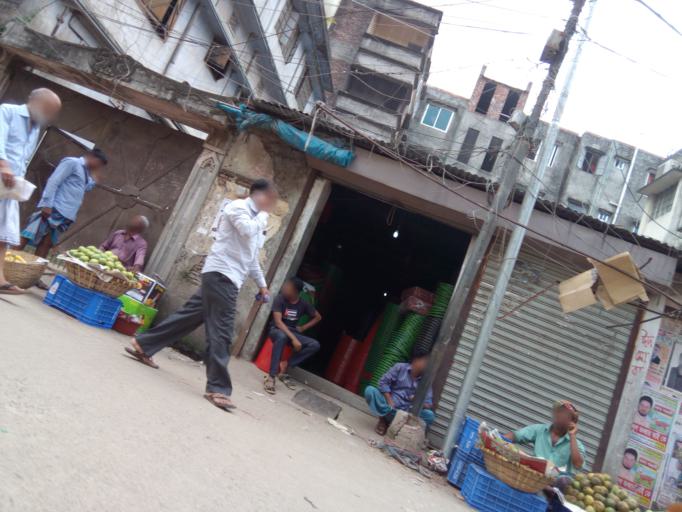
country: BD
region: Dhaka
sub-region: Dhaka
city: Dhaka
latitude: 23.7154
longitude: 90.4002
